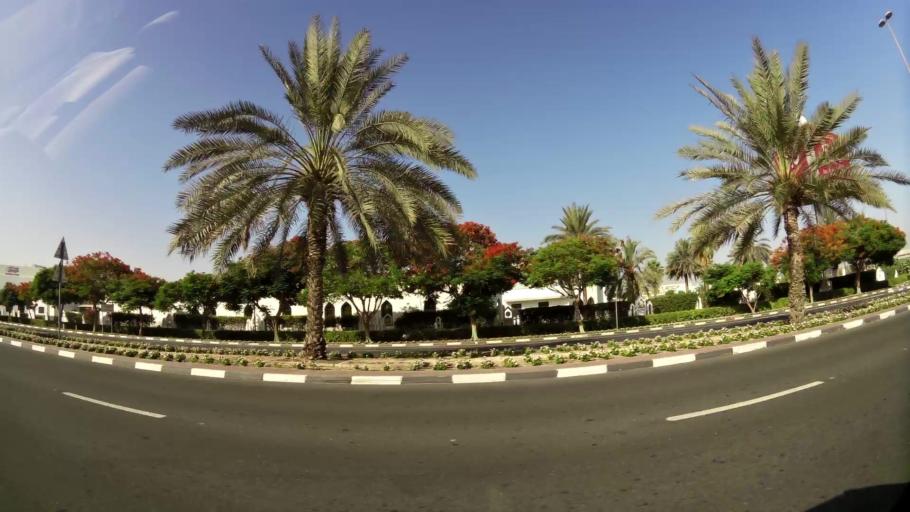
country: AE
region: Ash Shariqah
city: Sharjah
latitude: 25.2483
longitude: 55.3194
